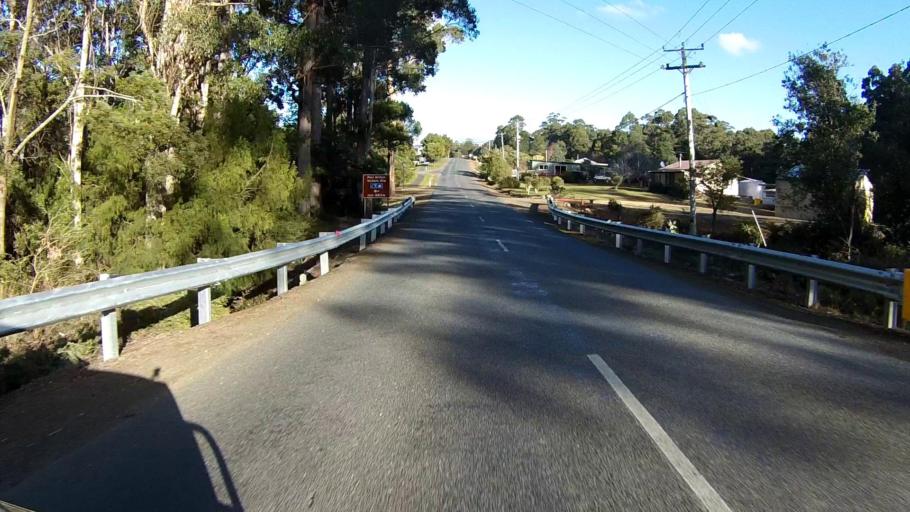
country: AU
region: Tasmania
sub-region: Clarence
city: Sandford
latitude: -43.1366
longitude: 147.8507
